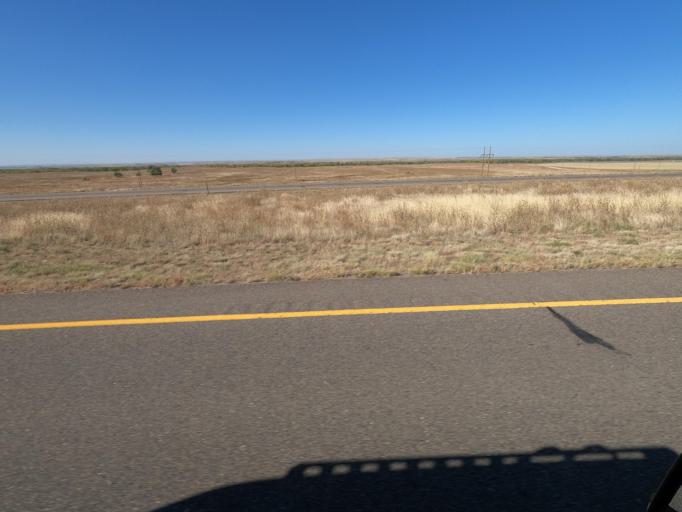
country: US
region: Nebraska
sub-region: Deuel County
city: Chappell
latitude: 40.8545
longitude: -102.6916
